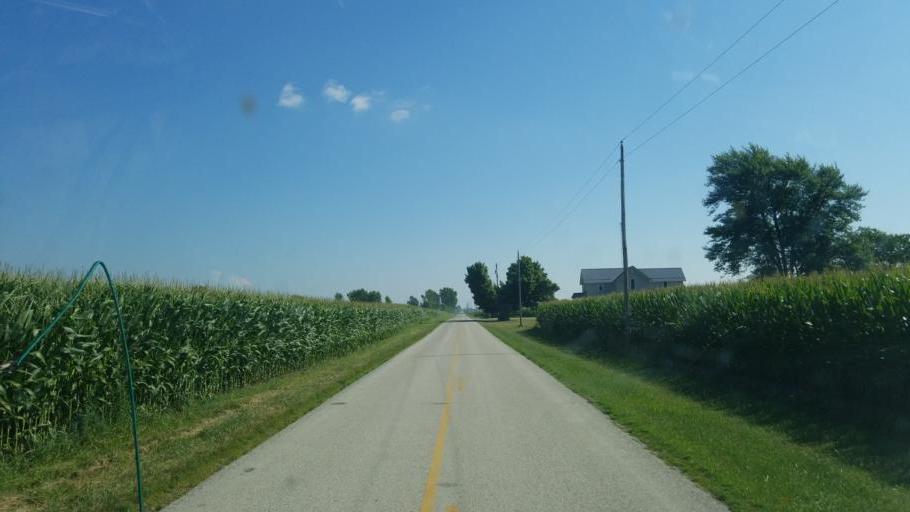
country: US
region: Ohio
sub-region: Hardin County
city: Kenton
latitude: 40.6868
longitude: -83.5143
